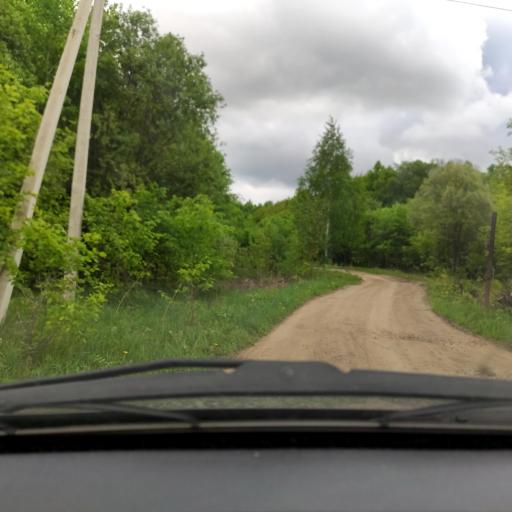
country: RU
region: Bashkortostan
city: Kabakovo
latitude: 54.7063
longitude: 56.1613
